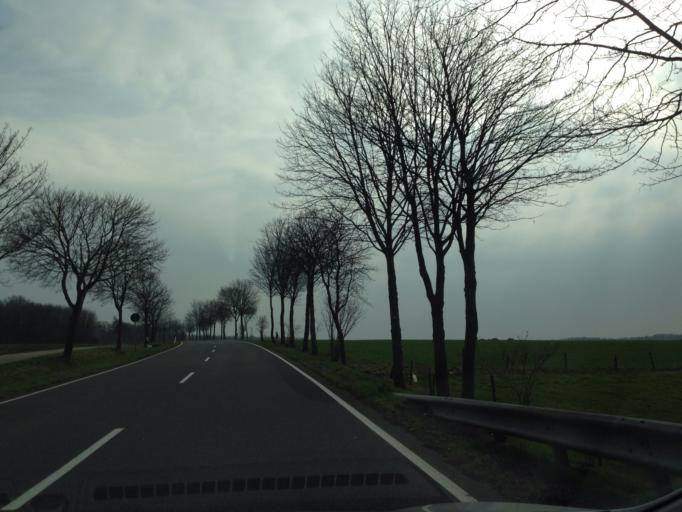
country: DE
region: North Rhine-Westphalia
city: Erkelenz
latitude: 51.0537
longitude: 6.2769
